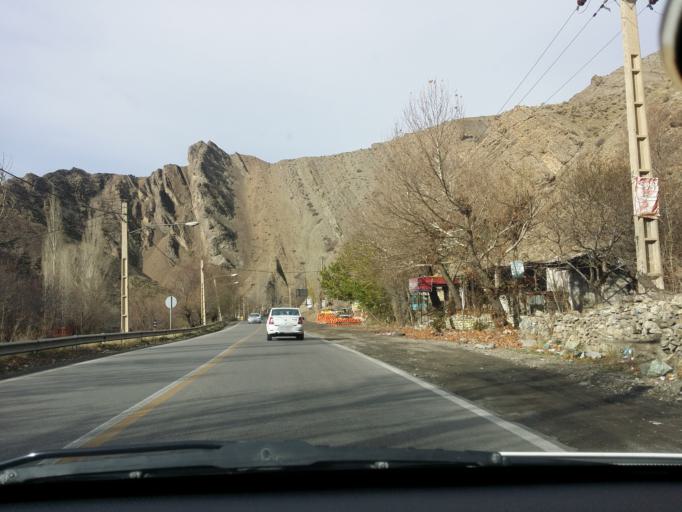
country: IR
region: Tehran
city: Tajrish
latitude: 36.0312
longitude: 51.2339
